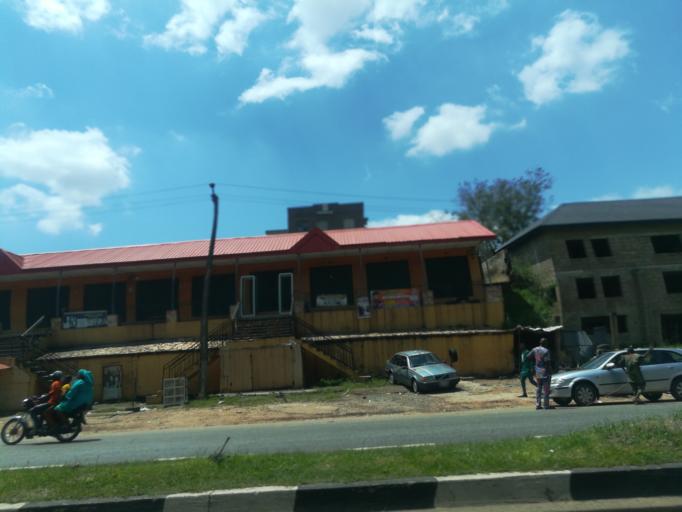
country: NG
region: Oyo
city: Ibadan
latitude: 7.3742
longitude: 3.8589
